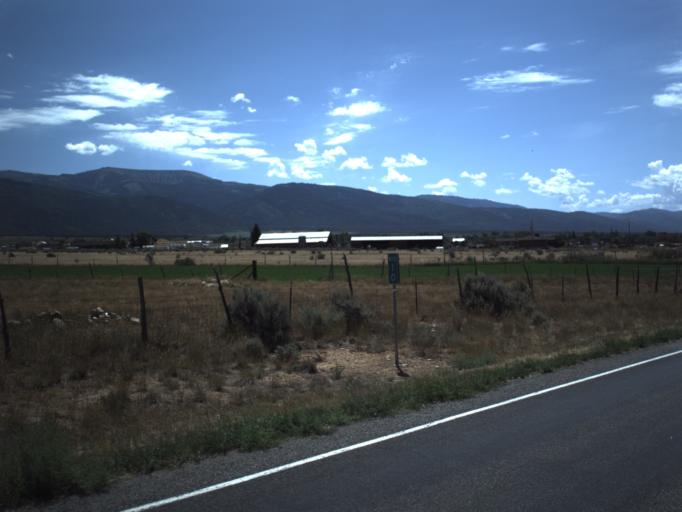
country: US
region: Utah
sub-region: Sanpete County
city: Mount Pleasant
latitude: 39.5020
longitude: -111.4877
